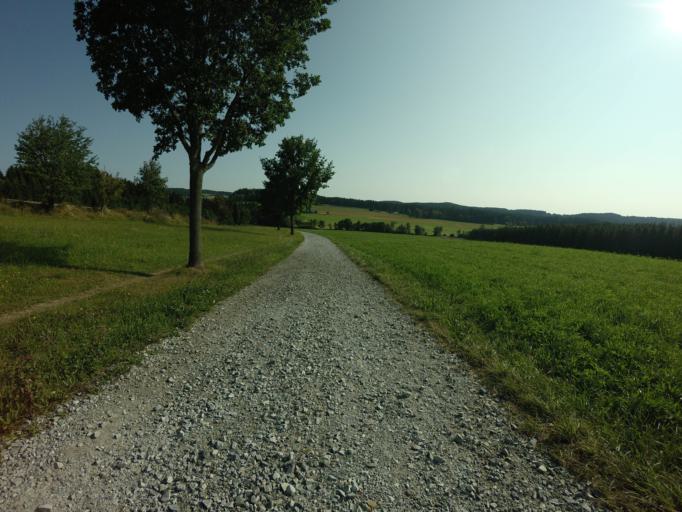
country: AT
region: Upper Austria
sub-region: Politischer Bezirk Urfahr-Umgebung
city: Bad Leonfelden
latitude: 48.5294
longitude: 14.3070
